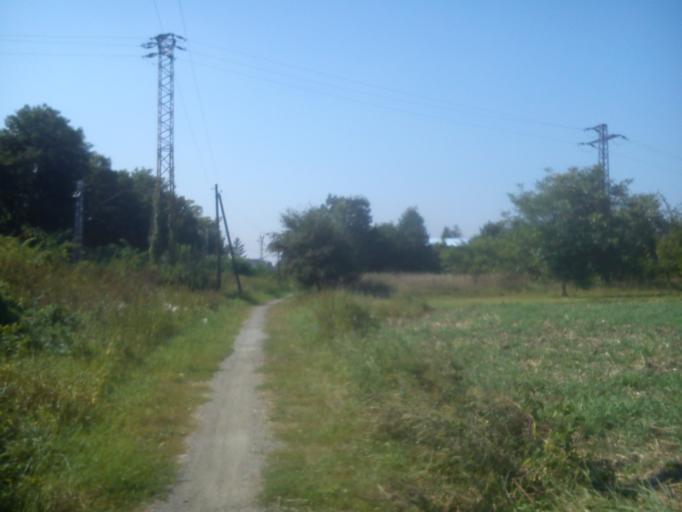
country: CZ
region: South Moravian
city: Sokolnice
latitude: 49.1074
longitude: 16.7411
